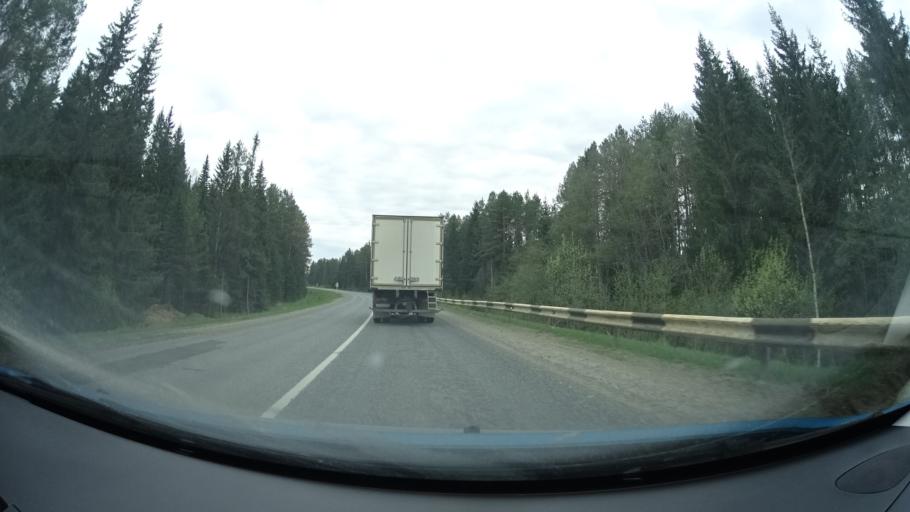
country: RU
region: Perm
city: Yugo-Kamskiy
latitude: 57.5621
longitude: 55.6789
